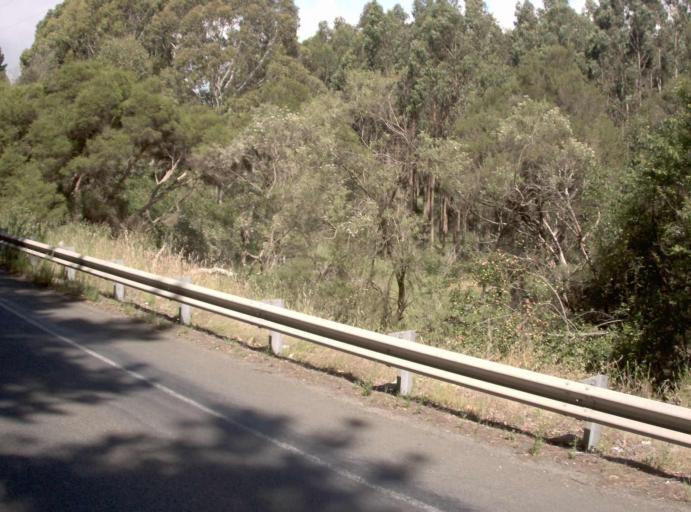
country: AU
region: Victoria
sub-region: Latrobe
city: Morwell
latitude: -38.1593
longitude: 146.4106
